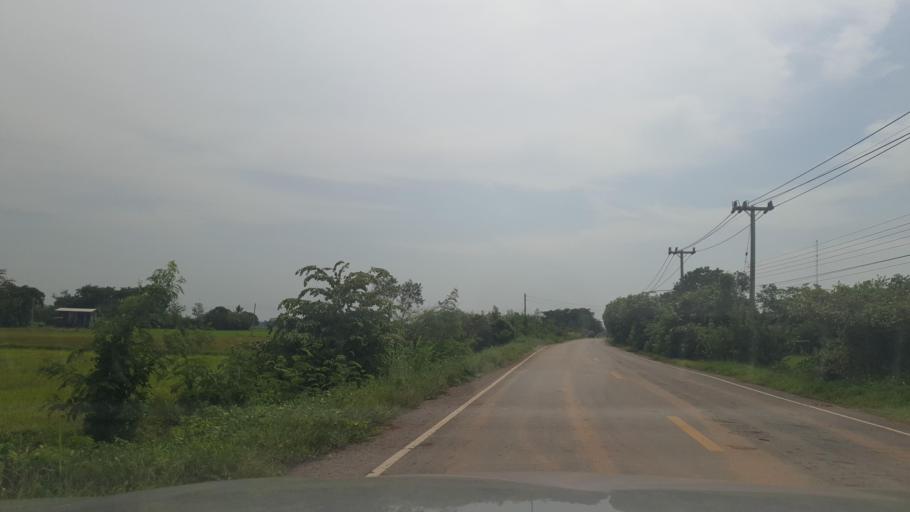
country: TH
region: Sukhothai
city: Si Samrong
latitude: 17.1164
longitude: 99.8805
